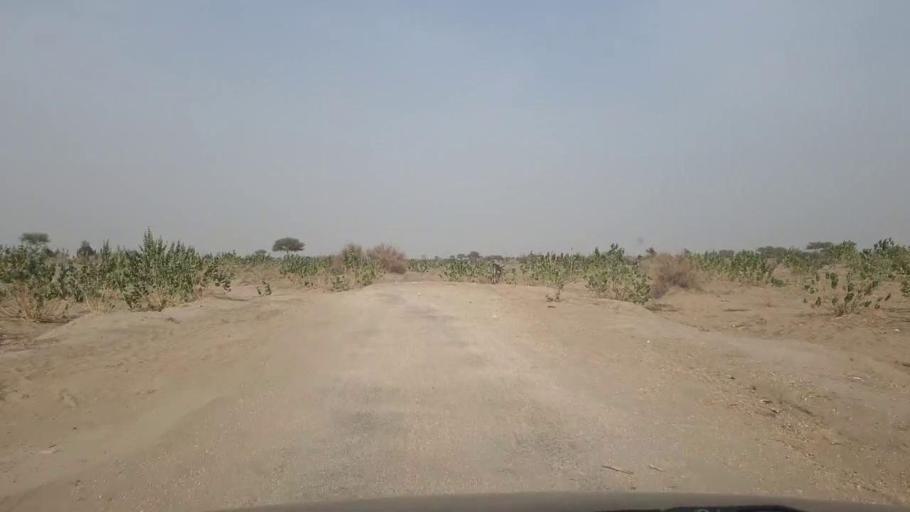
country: PK
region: Sindh
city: Chor
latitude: 25.6479
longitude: 69.9656
